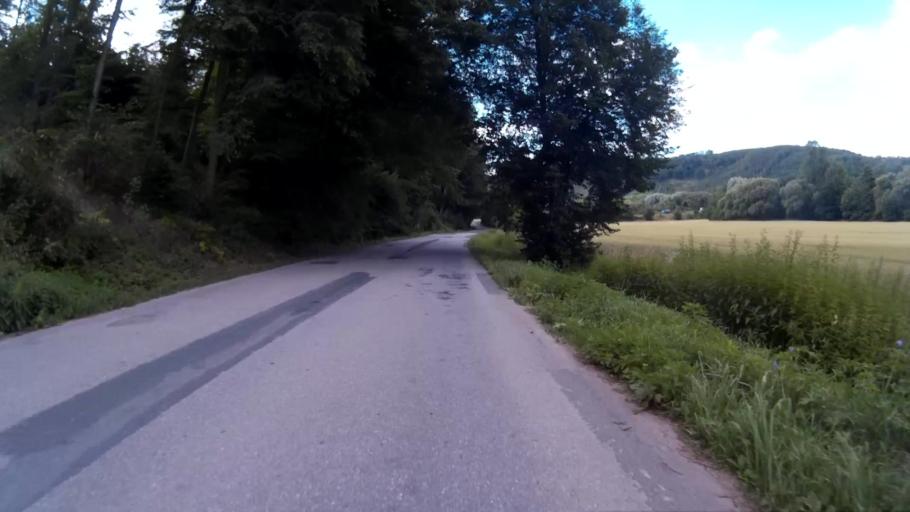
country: CZ
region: South Moravian
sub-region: Okres Brno-Venkov
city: Rosice
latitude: 49.1628
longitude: 16.4402
